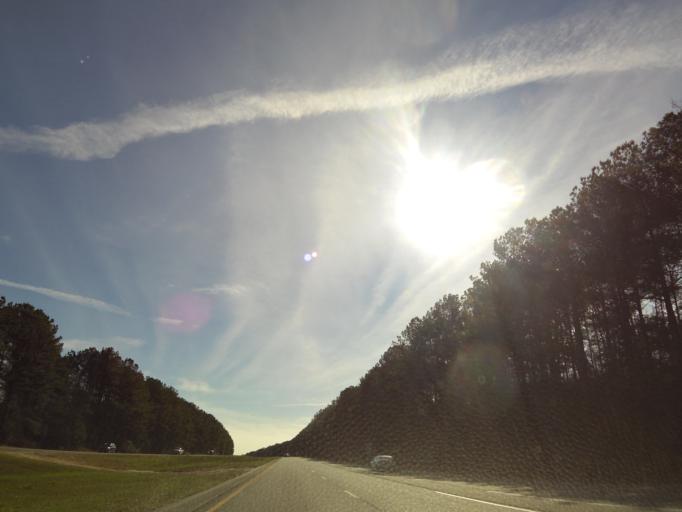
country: US
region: Alabama
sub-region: Russell County
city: Phenix City
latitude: 32.5993
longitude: -84.9547
